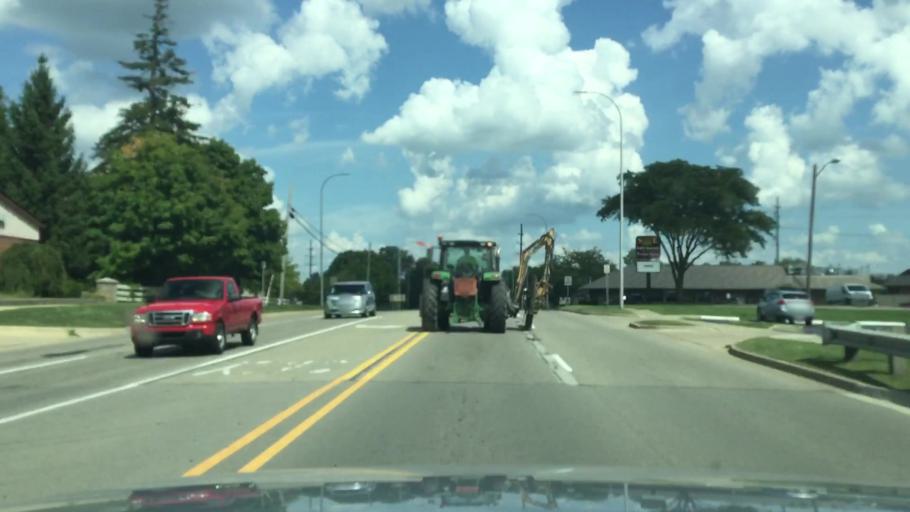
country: US
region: Michigan
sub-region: Washtenaw County
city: Saline
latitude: 42.1702
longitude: -83.7738
